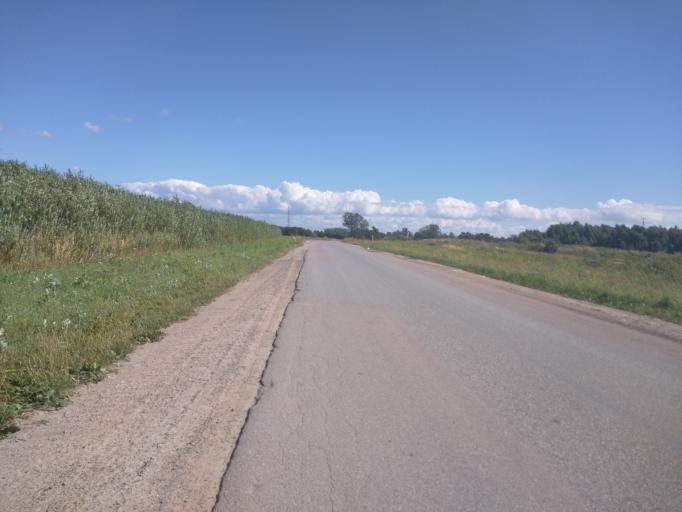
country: DK
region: Zealand
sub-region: Kalundborg Kommune
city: Svebolle
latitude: 55.6906
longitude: 11.2852
